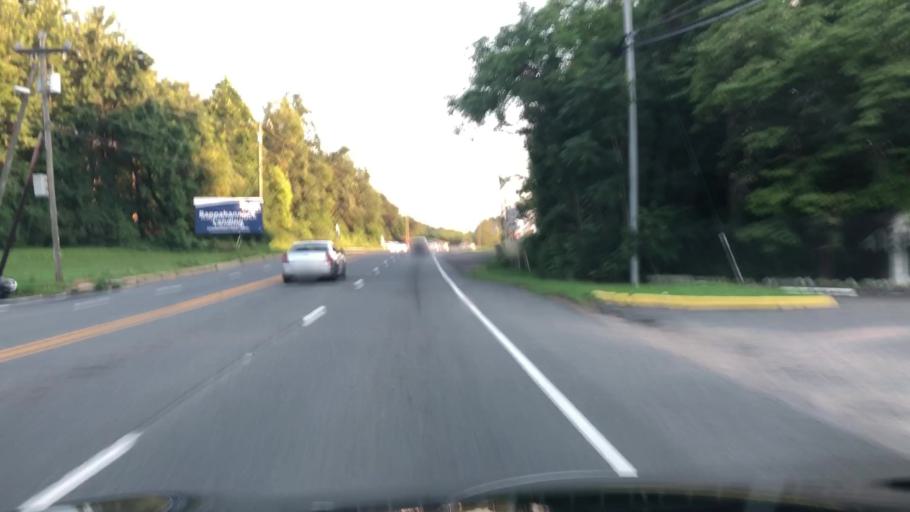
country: US
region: Virginia
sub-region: Stafford County
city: Falmouth
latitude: 38.3293
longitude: -77.4658
